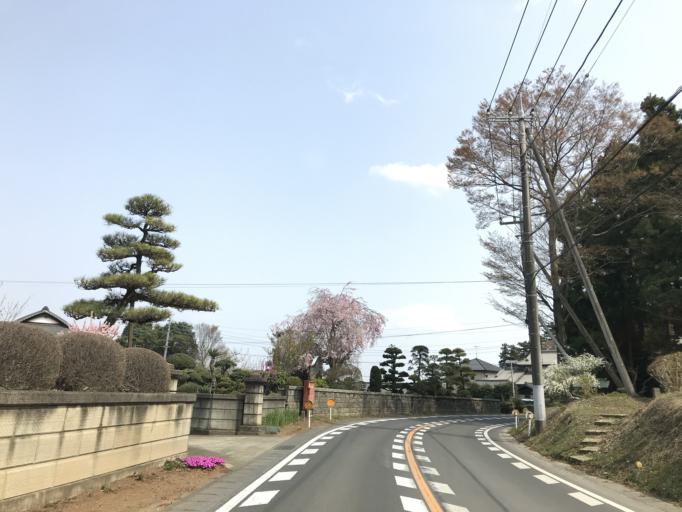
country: JP
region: Ibaraki
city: Ushiku
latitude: 36.0036
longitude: 140.0688
